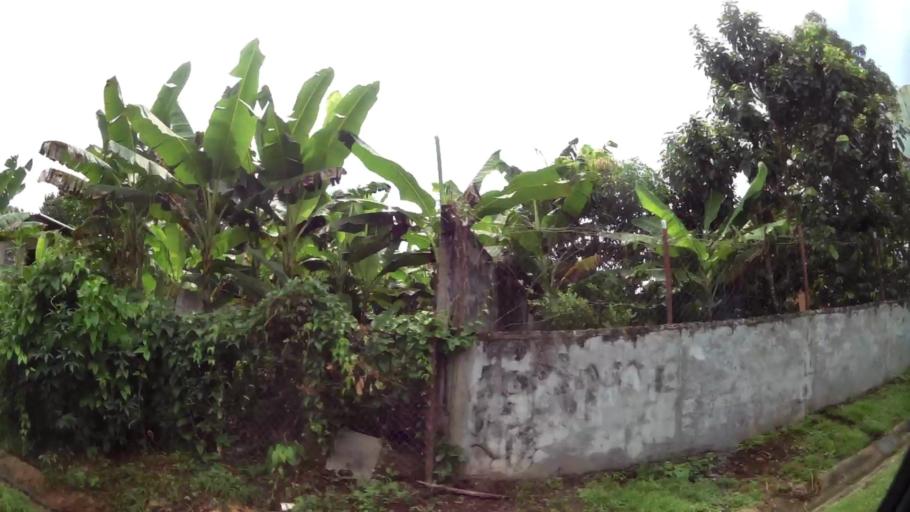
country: PA
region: Panama
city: Cabra Numero Uno
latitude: 9.1071
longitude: -79.3236
